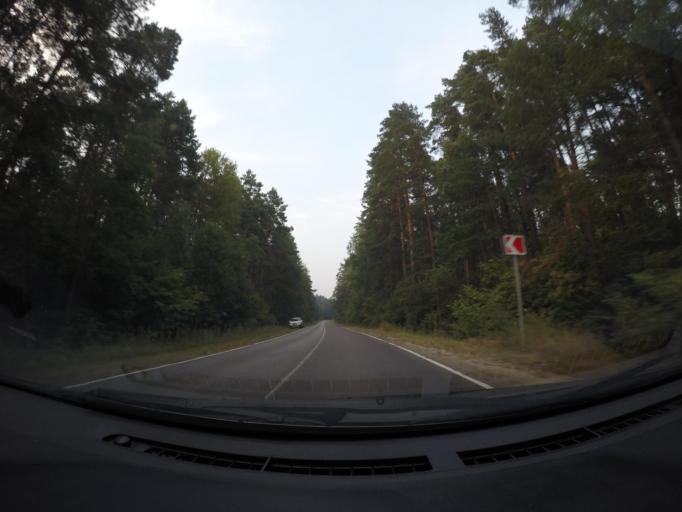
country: RU
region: Moskovskaya
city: Imeni Tsyurupy
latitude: 55.4985
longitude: 38.6948
